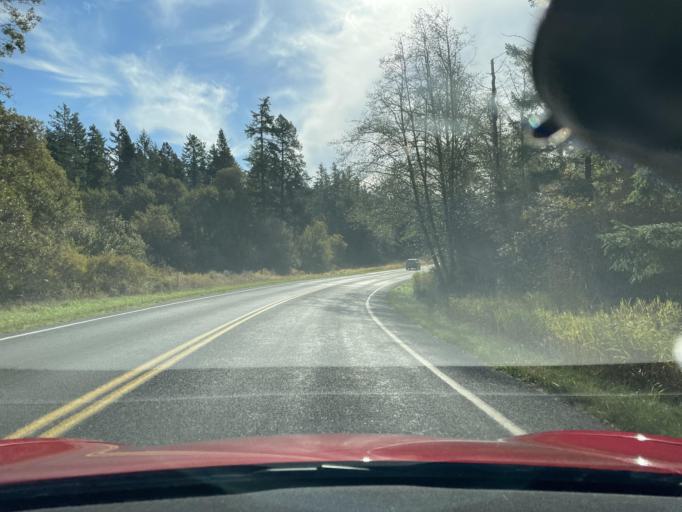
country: US
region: Washington
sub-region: San Juan County
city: Friday Harbor
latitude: 48.6030
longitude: -123.1325
